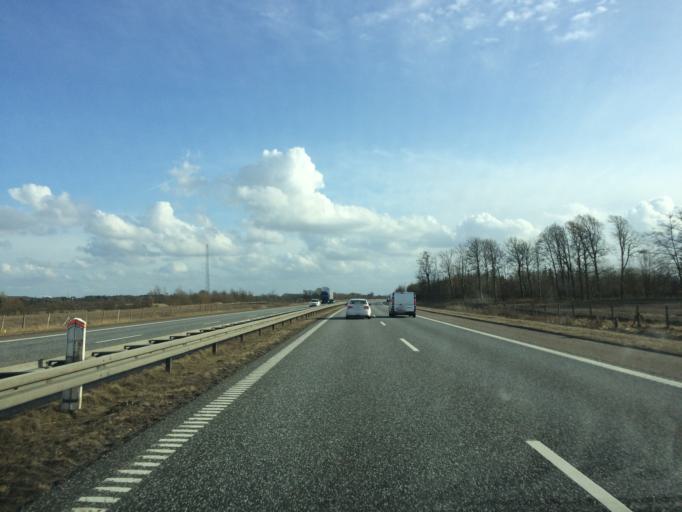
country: DK
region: North Denmark
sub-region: Alborg Kommune
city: Vestbjerg
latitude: 57.1539
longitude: 9.9456
